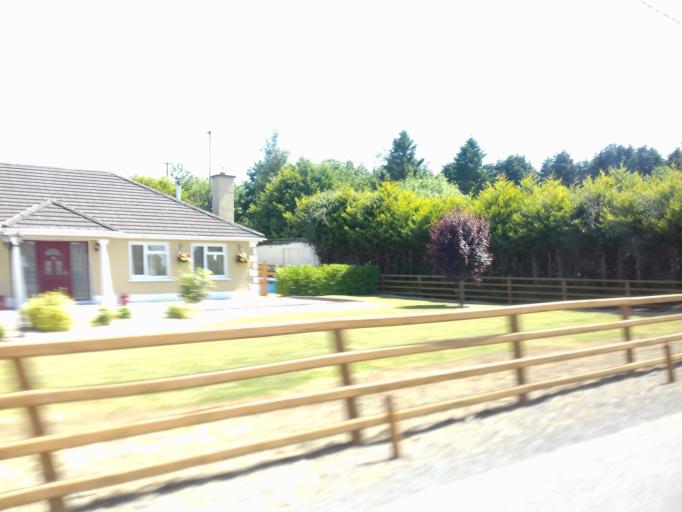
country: IE
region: Leinster
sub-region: An Mhi
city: Stamullin
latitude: 53.5783
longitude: -6.3112
